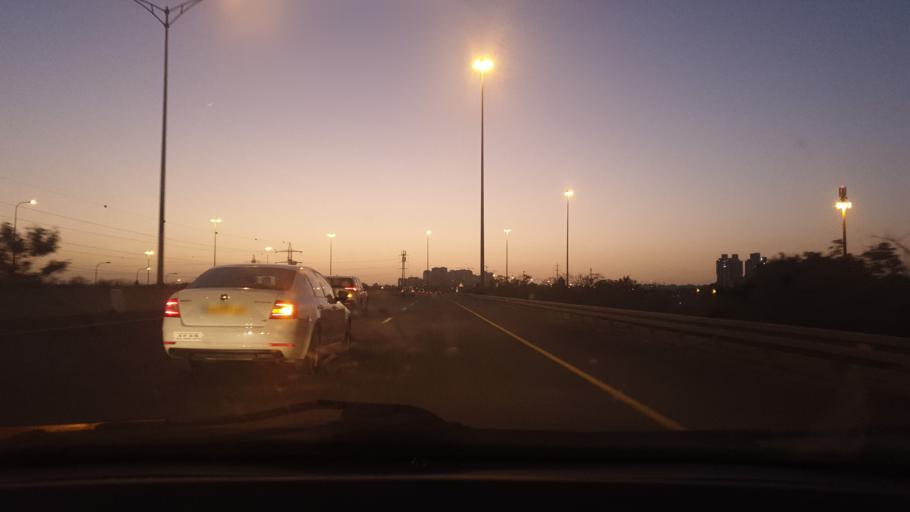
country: IL
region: Central District
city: Nehalim
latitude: 32.0669
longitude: 34.9063
